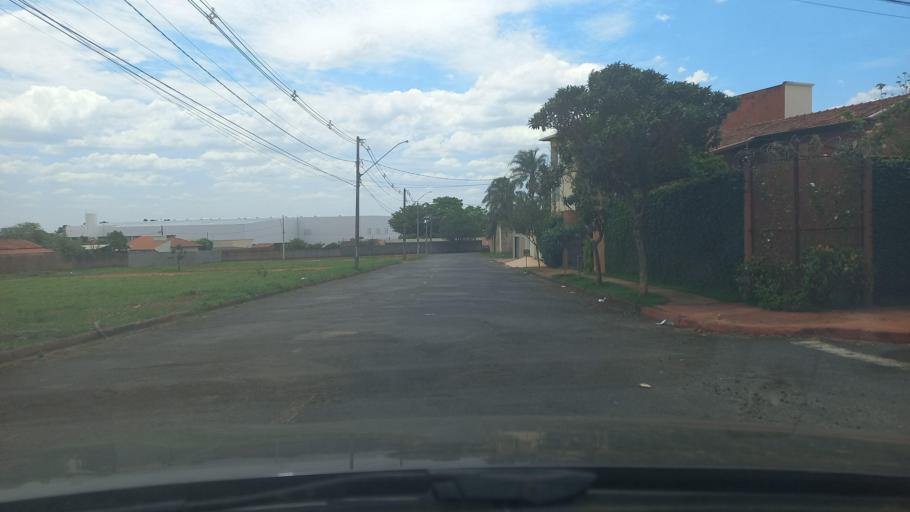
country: BR
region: Minas Gerais
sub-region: Uberaba
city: Uberaba
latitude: -19.7522
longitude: -47.9700
